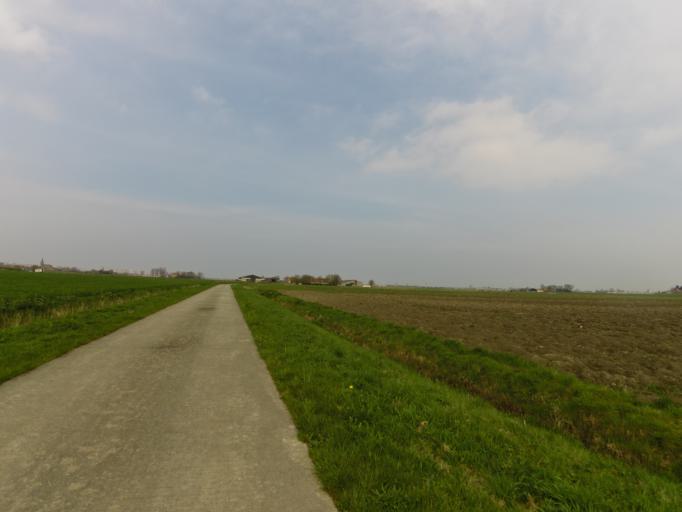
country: BE
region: Flanders
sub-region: Provincie West-Vlaanderen
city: Middelkerke
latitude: 51.1776
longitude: 2.8512
